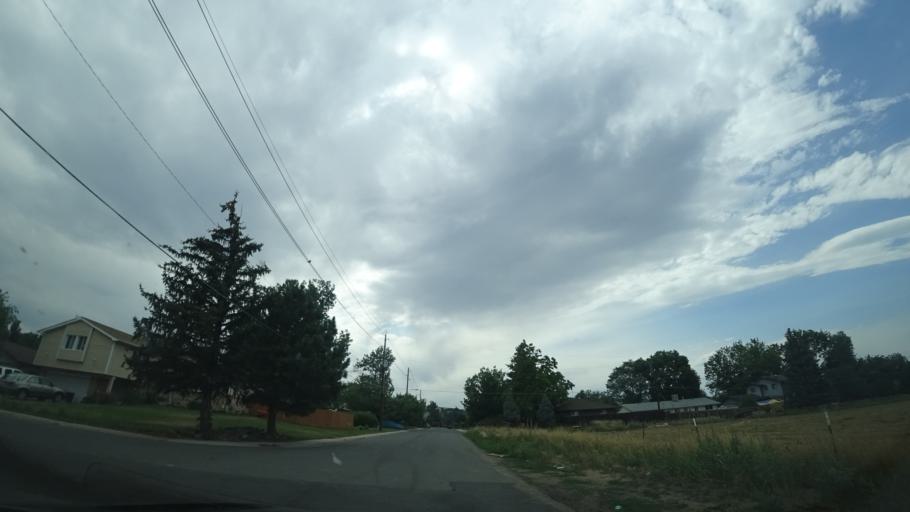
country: US
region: Colorado
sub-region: Jefferson County
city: Lakewood
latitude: 39.7094
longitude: -105.1018
